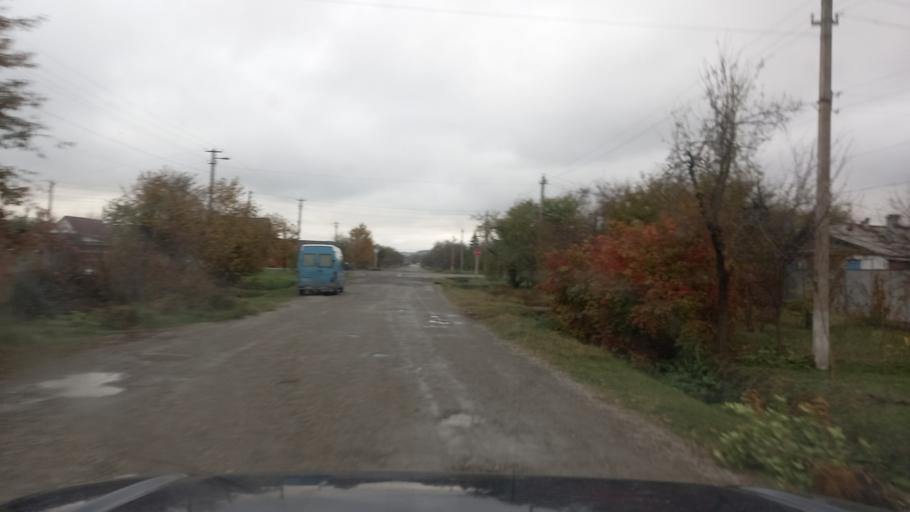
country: RU
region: Adygeya
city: Maykop
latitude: 44.6197
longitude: 40.1263
